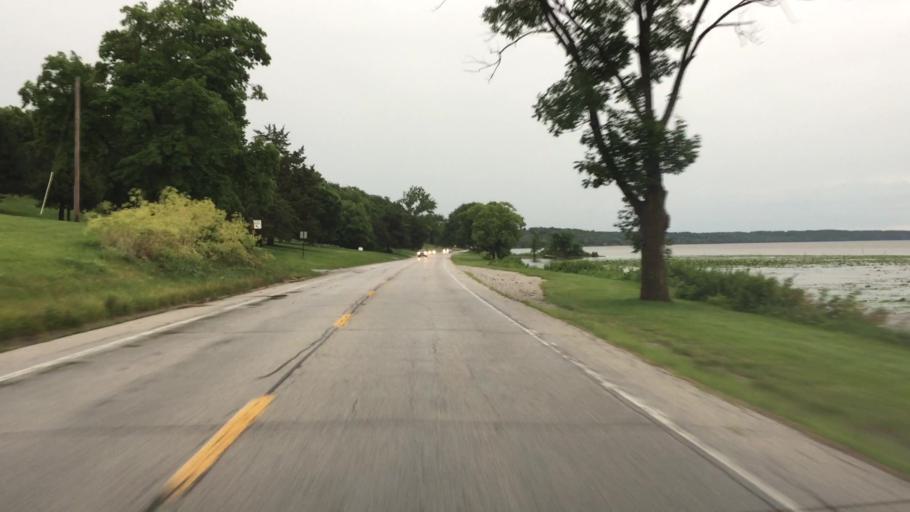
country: US
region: Illinois
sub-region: Hancock County
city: Nauvoo
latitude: 40.5270
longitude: -91.3695
